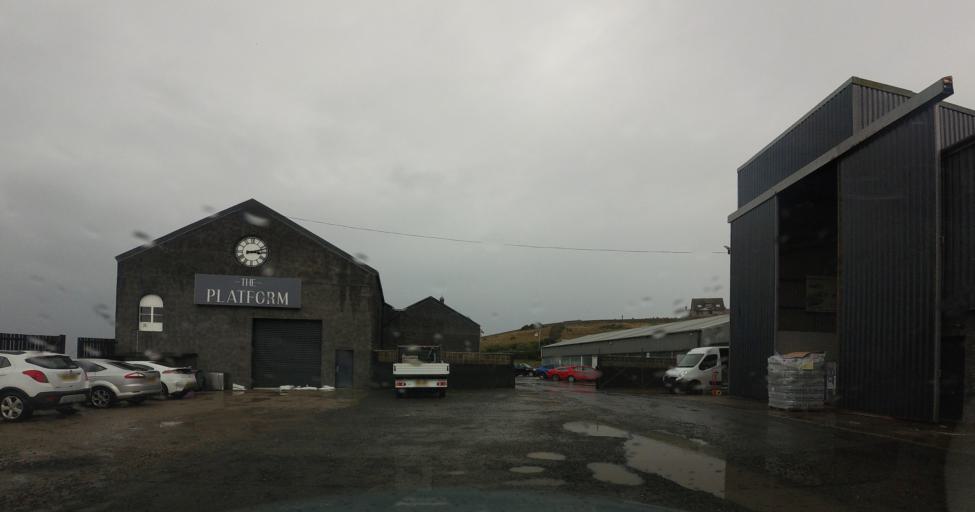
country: GB
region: Scotland
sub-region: Aberdeenshire
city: Macduff
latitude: 57.6668
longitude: -2.5043
